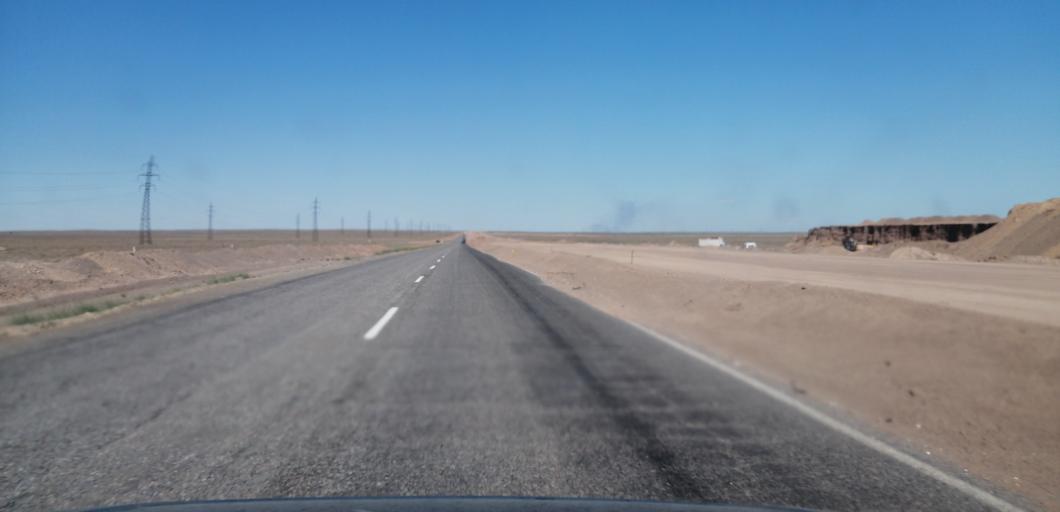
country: KZ
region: Qaraghandy
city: Balqash
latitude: 46.7947
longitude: 74.6545
